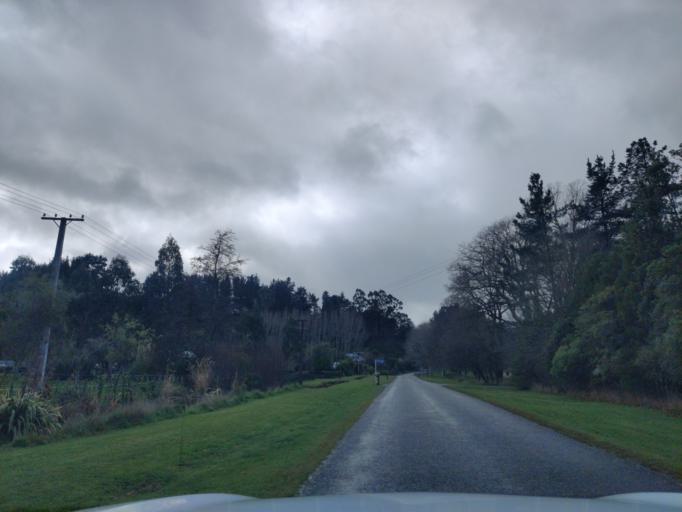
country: NZ
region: Manawatu-Wanganui
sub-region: Palmerston North City
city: Palmerston North
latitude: -40.1694
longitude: 175.8002
